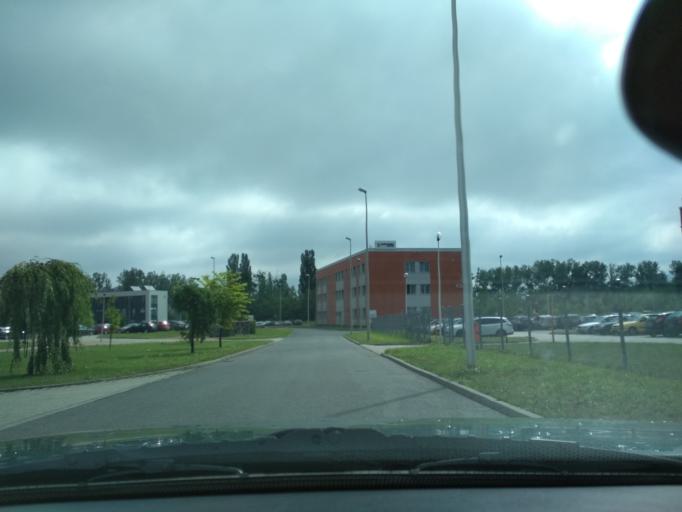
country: PL
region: Silesian Voivodeship
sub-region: Gliwice
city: Gliwice
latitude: 50.2765
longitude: 18.6823
